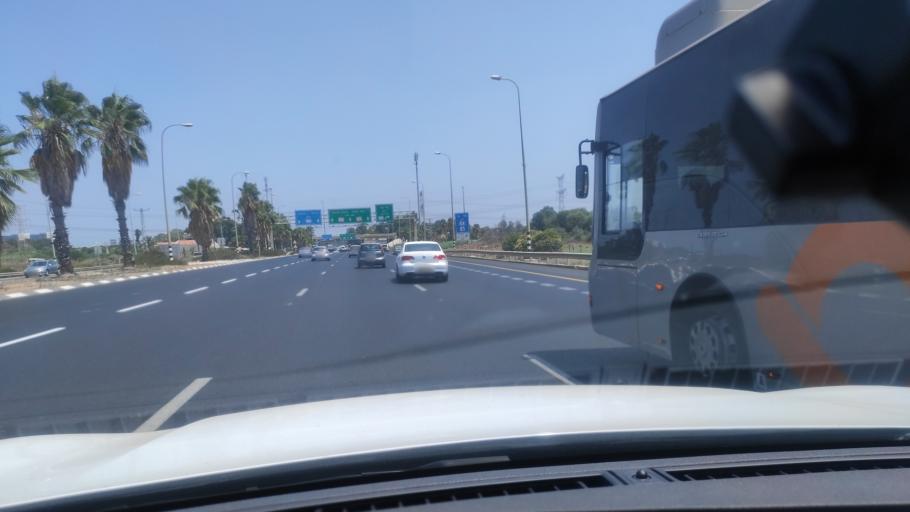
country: IL
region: Central District
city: Petah Tiqwa
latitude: 32.1176
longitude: 34.9033
